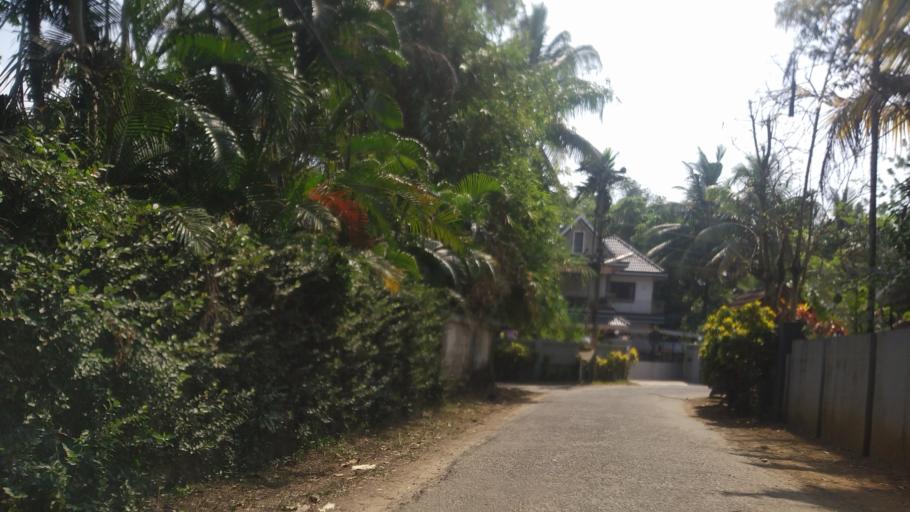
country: IN
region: Kerala
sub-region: Ernakulam
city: Elur
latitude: 10.1294
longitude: 76.2328
